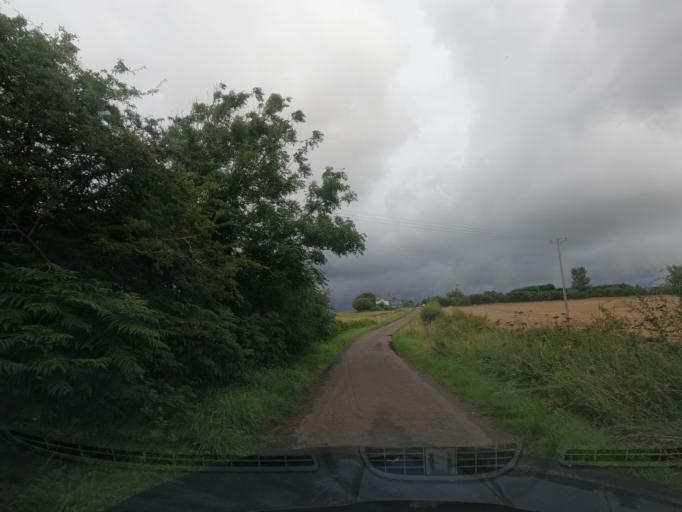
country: GB
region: England
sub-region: Northumberland
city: Ancroft
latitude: 55.7274
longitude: -2.0269
